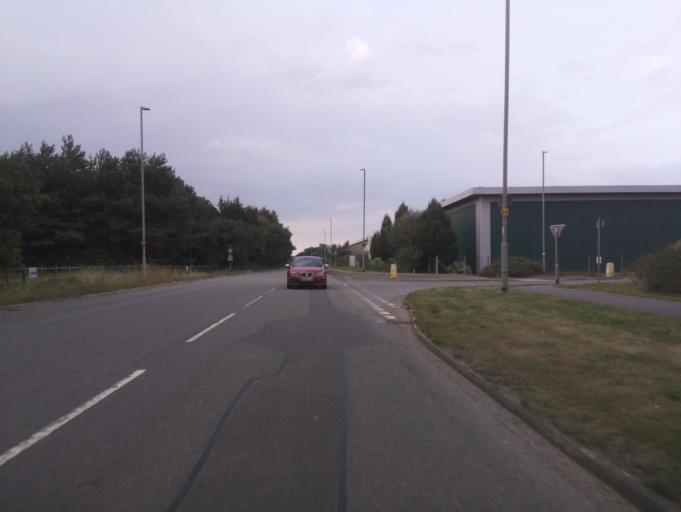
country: GB
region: England
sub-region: Nottinghamshire
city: South Collingham
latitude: 53.1509
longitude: -0.6702
